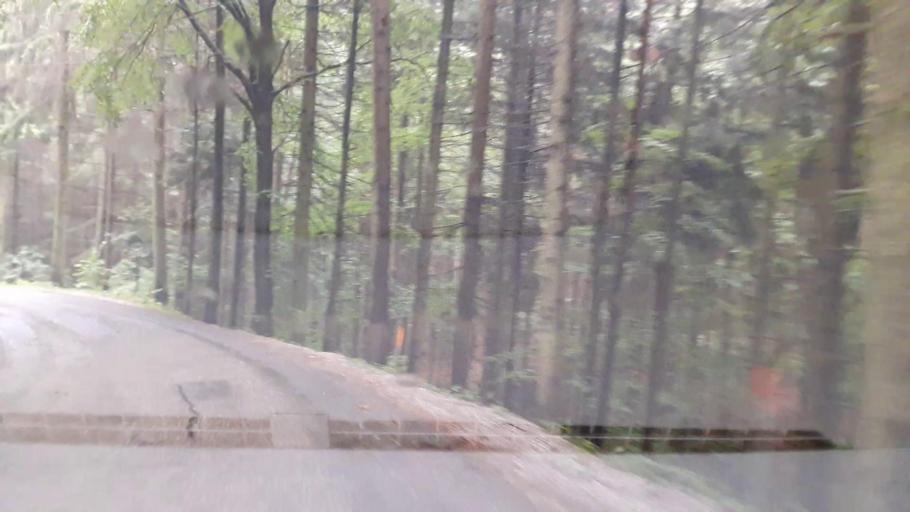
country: AT
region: Lower Austria
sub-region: Politischer Bezirk Krems
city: Aggsbach
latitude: 48.2920
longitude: 15.3684
